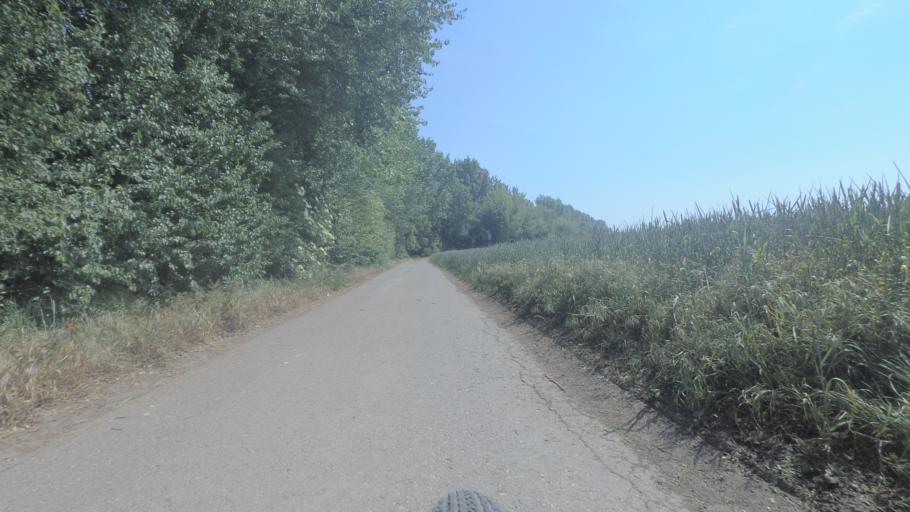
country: DE
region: Saxony-Anhalt
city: Gross Bornecke
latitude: 51.8533
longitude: 11.4749
